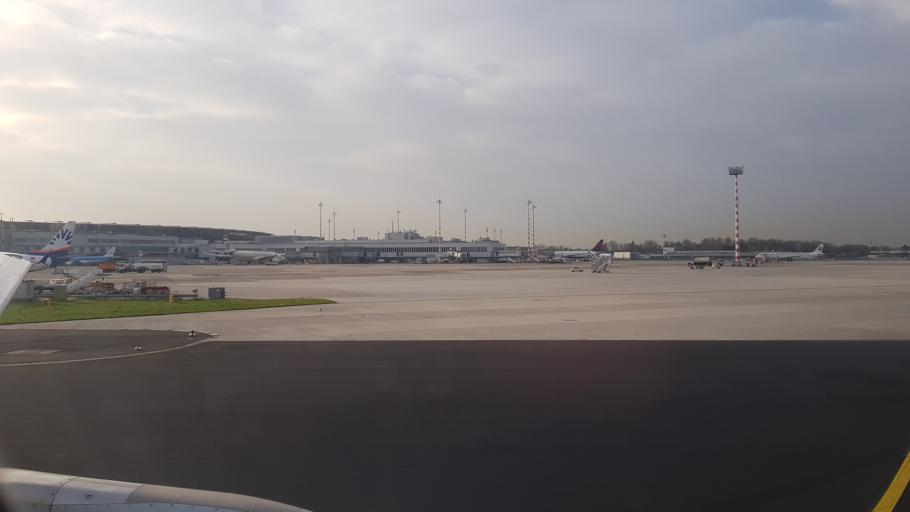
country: DE
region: North Rhine-Westphalia
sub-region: Regierungsbezirk Dusseldorf
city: Dusseldorf
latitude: 51.2804
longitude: 6.7582
